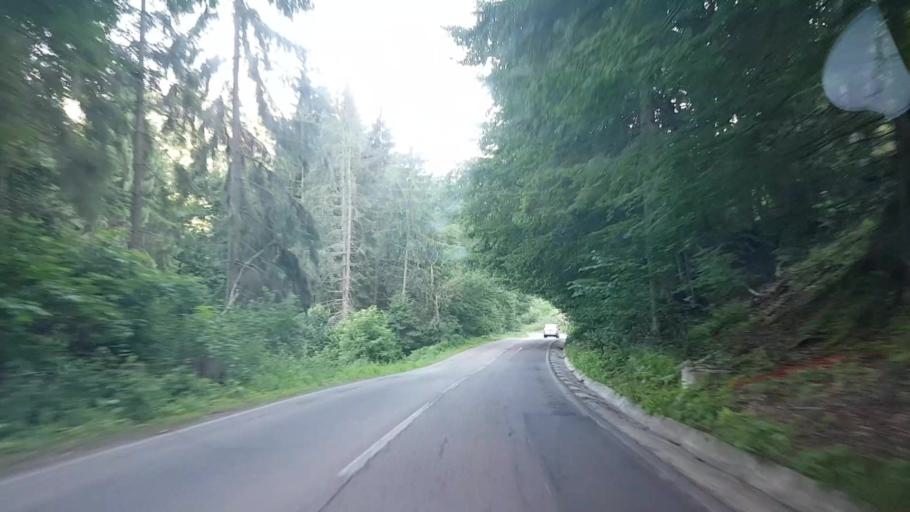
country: RO
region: Harghita
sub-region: Comuna Praid
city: Ocna de Sus
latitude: 46.5859
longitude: 25.2437
